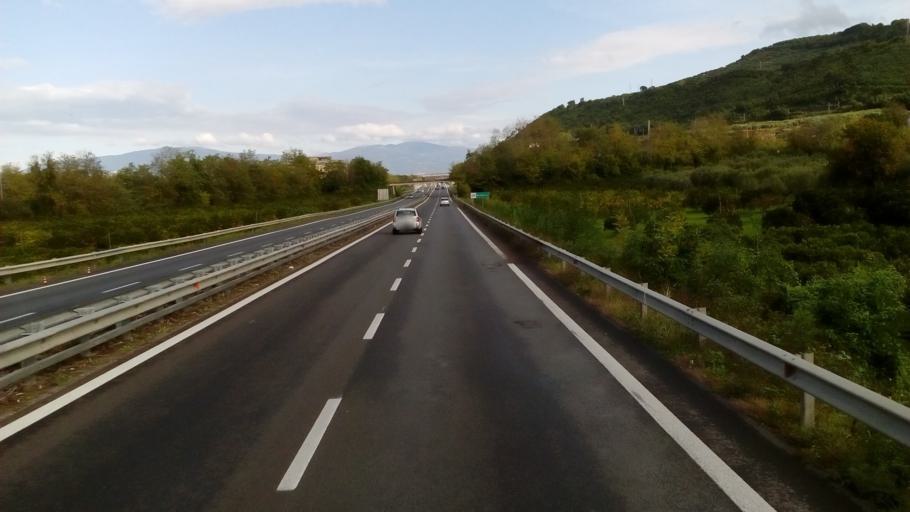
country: IT
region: Calabria
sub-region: Provincia di Vibo-Valentia
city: Pizzo
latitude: 38.7750
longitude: 16.2151
